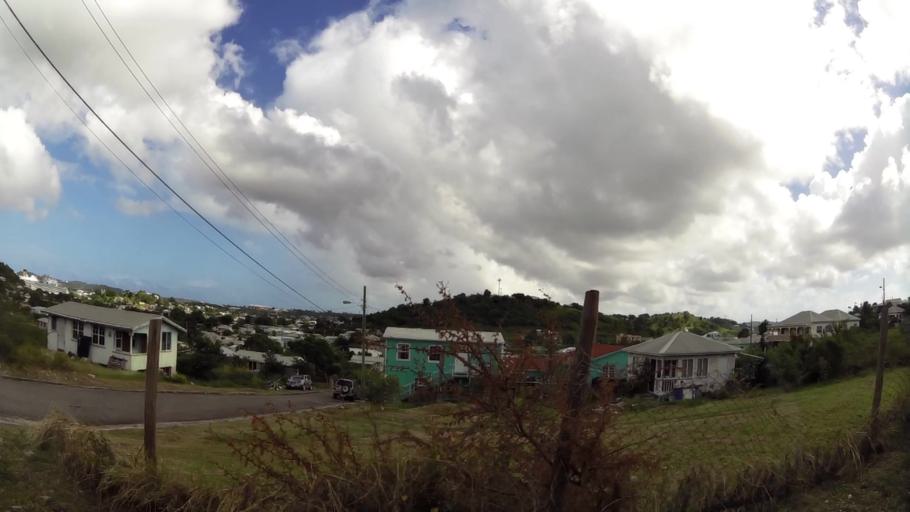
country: AG
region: Saint John
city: Saint John's
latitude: 17.1107
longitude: -61.8565
